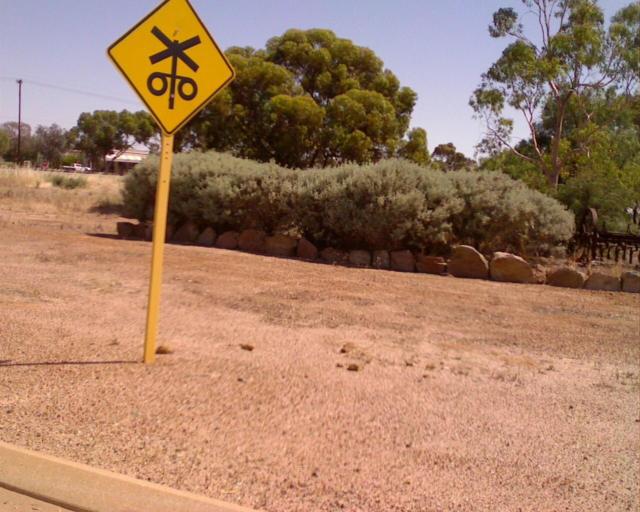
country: AU
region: Western Australia
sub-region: Merredin
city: Merredin
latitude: -31.6107
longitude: 117.8772
